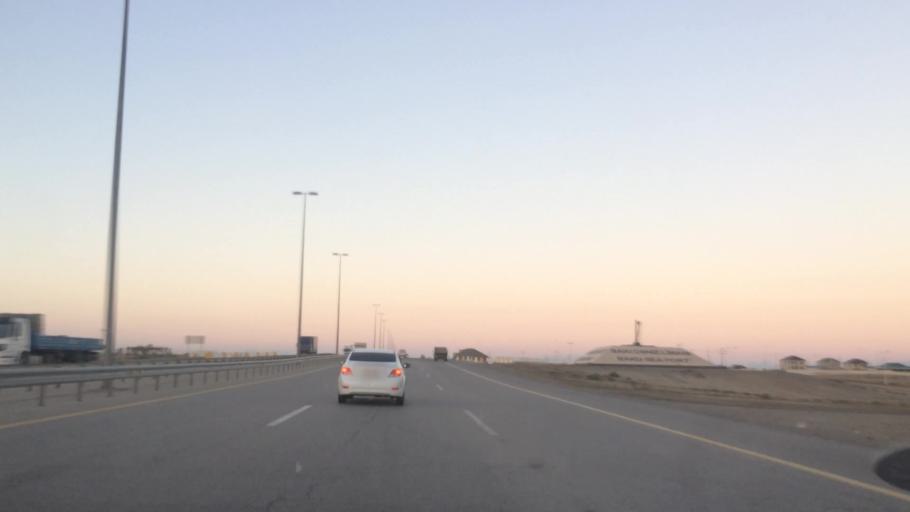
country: AZ
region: Baki
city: Qobustan
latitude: 39.9807
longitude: 49.4227
